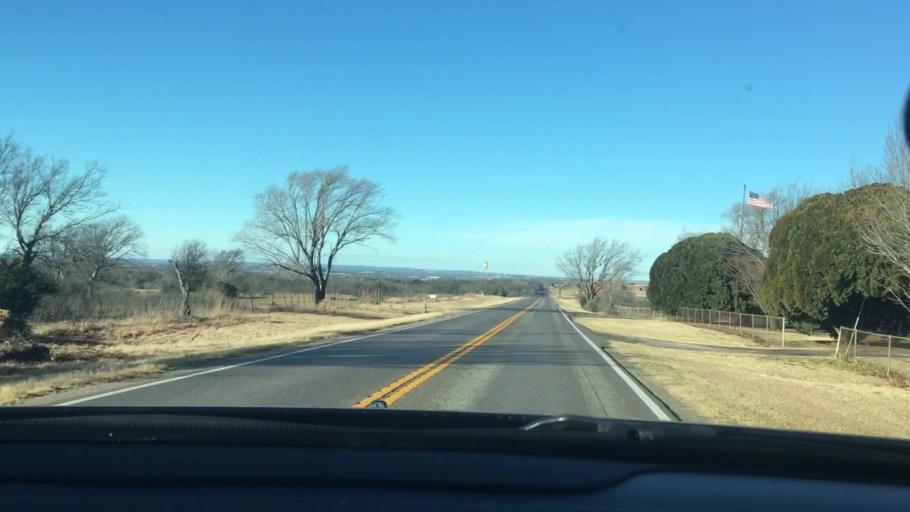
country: US
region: Oklahoma
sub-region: Murray County
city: Sulphur
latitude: 34.5109
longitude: -96.9346
